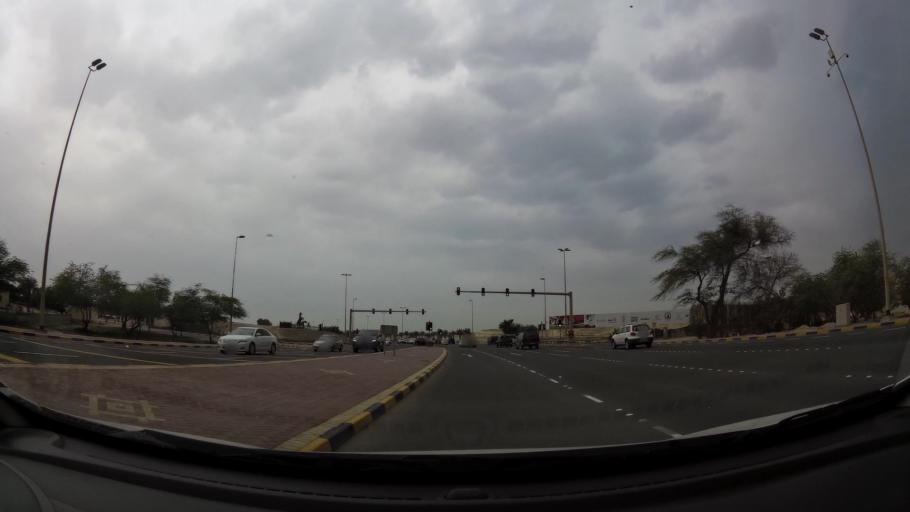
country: BH
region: Central Governorate
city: Dar Kulayb
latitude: 26.0714
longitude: 50.5251
